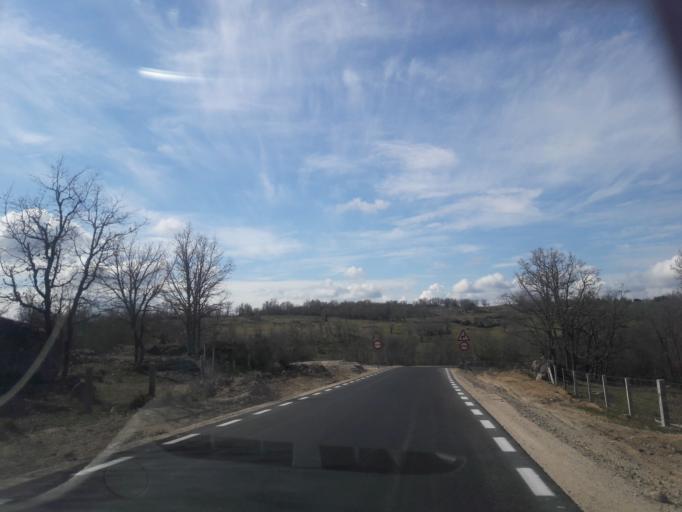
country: ES
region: Castille and Leon
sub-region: Provincia de Salamanca
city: Monleon
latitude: 40.5313
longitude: -5.8300
